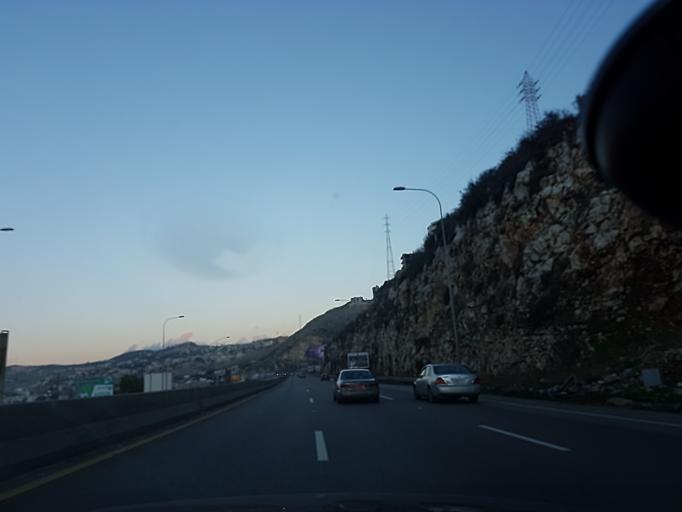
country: LB
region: Liban-Sud
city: Sidon
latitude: 33.6489
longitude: 35.4084
